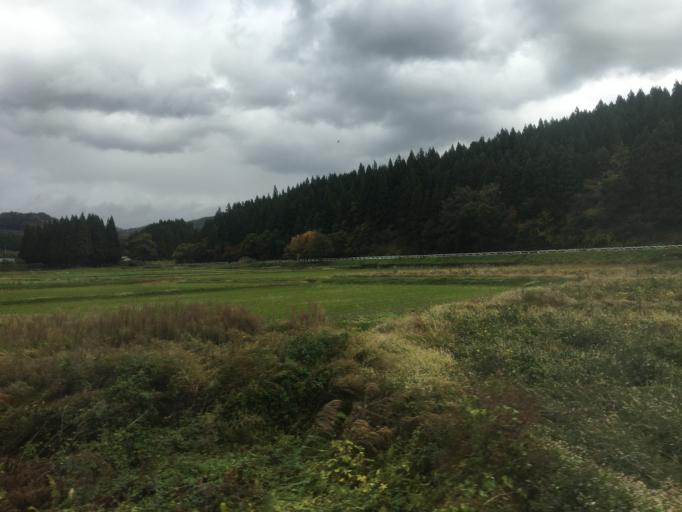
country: JP
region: Yamagata
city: Nagai
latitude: 38.0506
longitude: 139.7587
